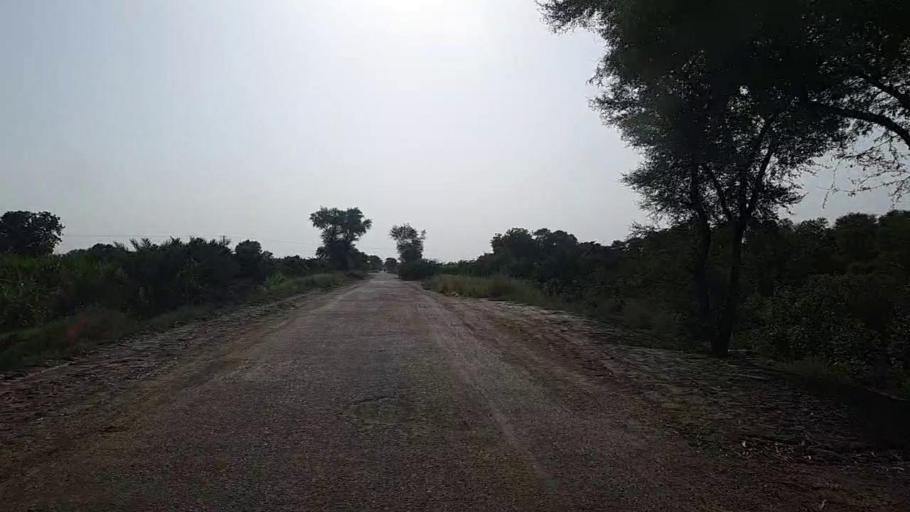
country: PK
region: Sindh
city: Pad Idan
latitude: 26.8532
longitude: 68.3264
